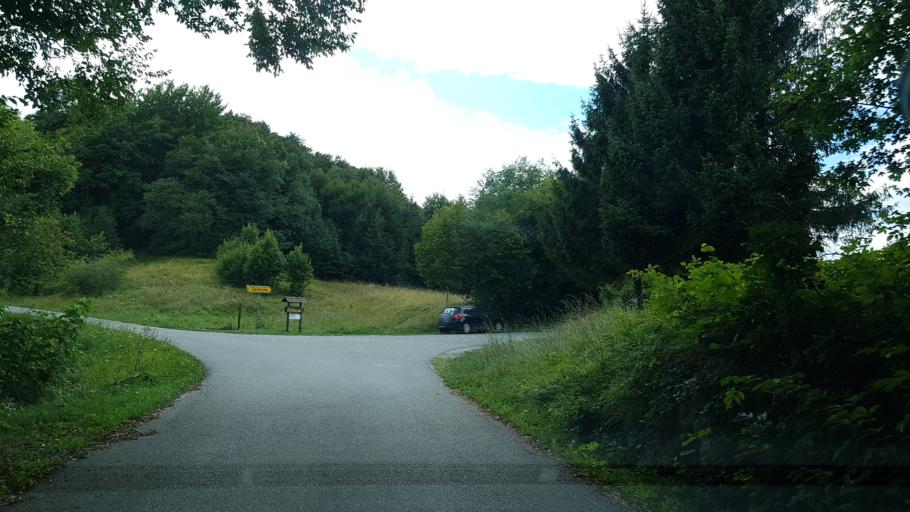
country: SI
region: Kanal
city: Deskle
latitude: 46.0688
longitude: 13.5725
